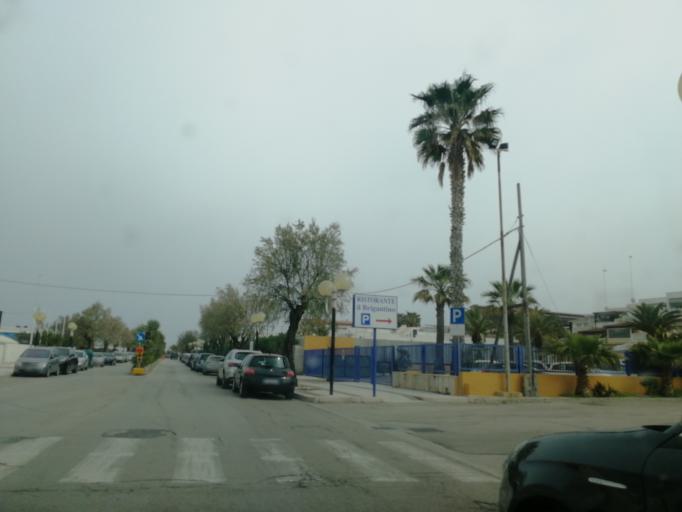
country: IT
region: Apulia
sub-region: Provincia di Barletta - Andria - Trani
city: Barletta
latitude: 41.3207
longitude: 16.2965
